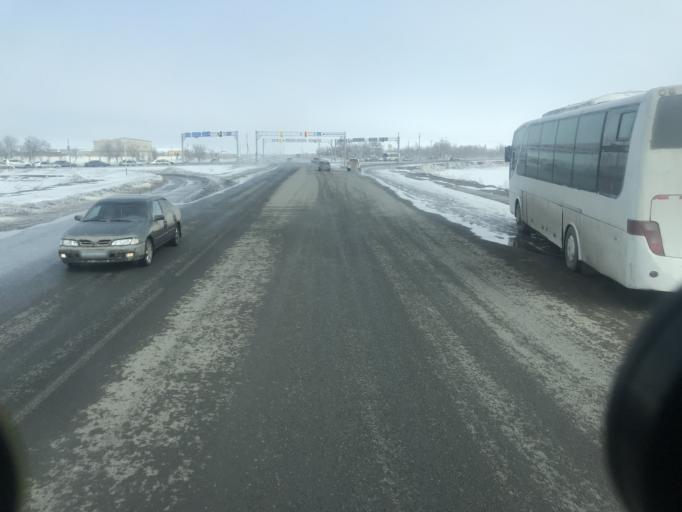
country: KZ
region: Aqtoebe
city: Aqtobe
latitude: 50.2894
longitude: 57.2885
